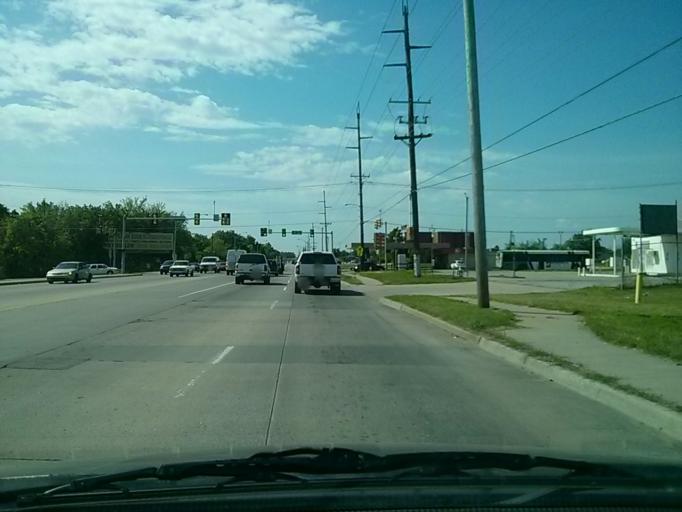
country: US
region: Oklahoma
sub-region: Tulsa County
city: Turley
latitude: 36.2069
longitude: -95.9757
